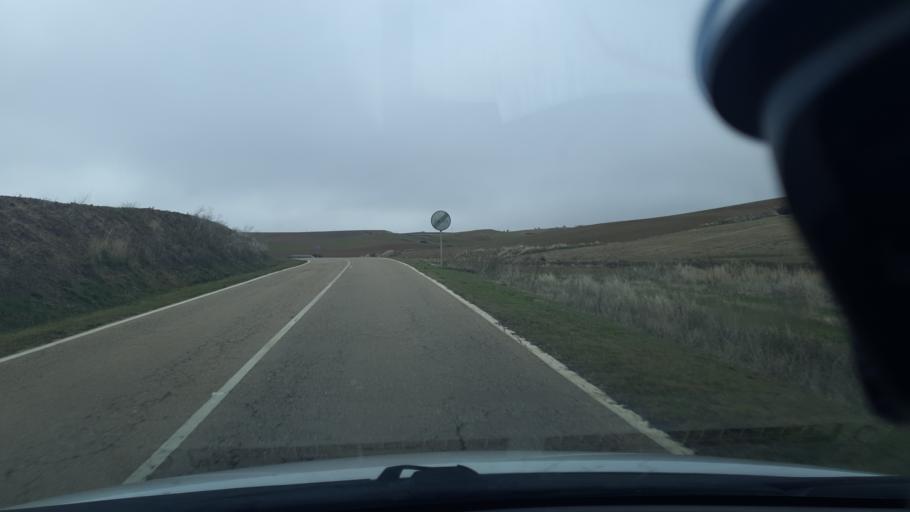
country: ES
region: Castille and Leon
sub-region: Provincia de Segovia
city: Hontanares de Eresma
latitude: 40.9872
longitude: -4.2017
